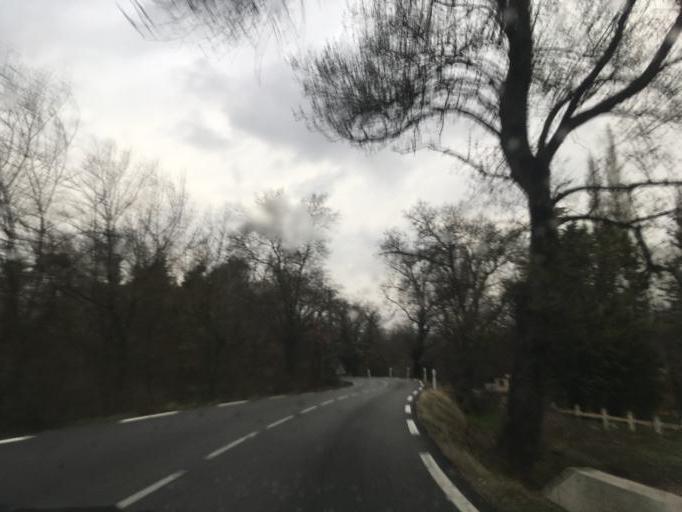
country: FR
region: Provence-Alpes-Cote d'Azur
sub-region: Departement du Var
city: Forcalqueiret
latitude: 43.3387
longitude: 6.0992
